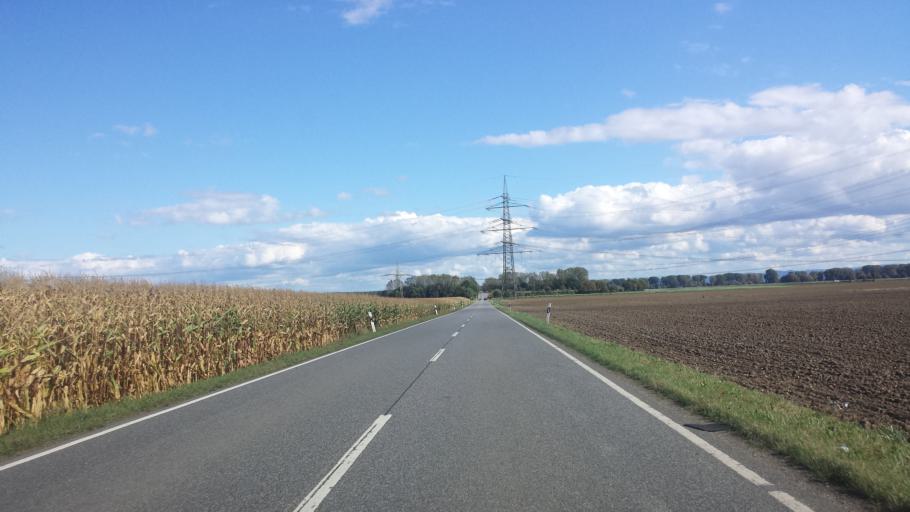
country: DE
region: Rheinland-Pfalz
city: Bobenheim-Roxheim
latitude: 49.5681
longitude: 8.3857
